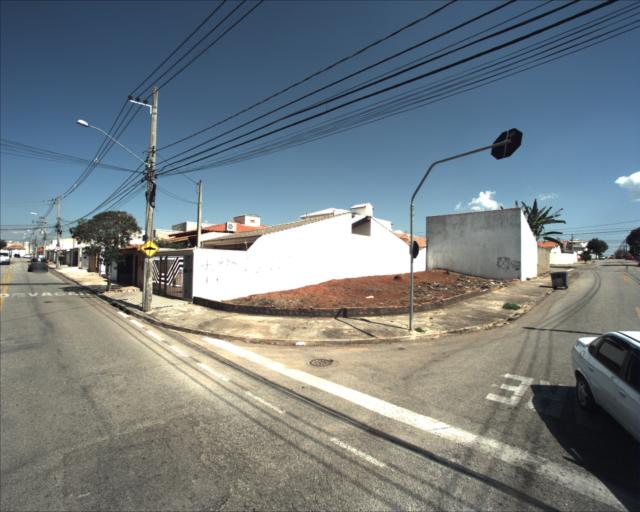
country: BR
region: Sao Paulo
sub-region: Sorocaba
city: Sorocaba
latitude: -23.5096
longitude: -47.5133
